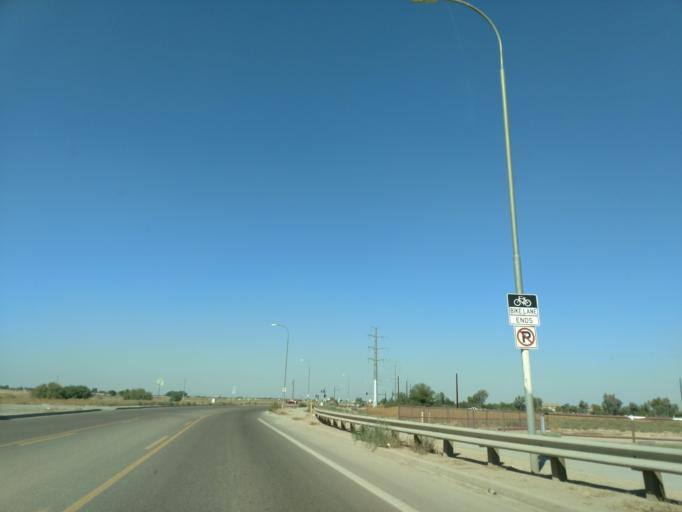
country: US
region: Arizona
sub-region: Maricopa County
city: Laveen
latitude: 33.3751
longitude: -112.1847
